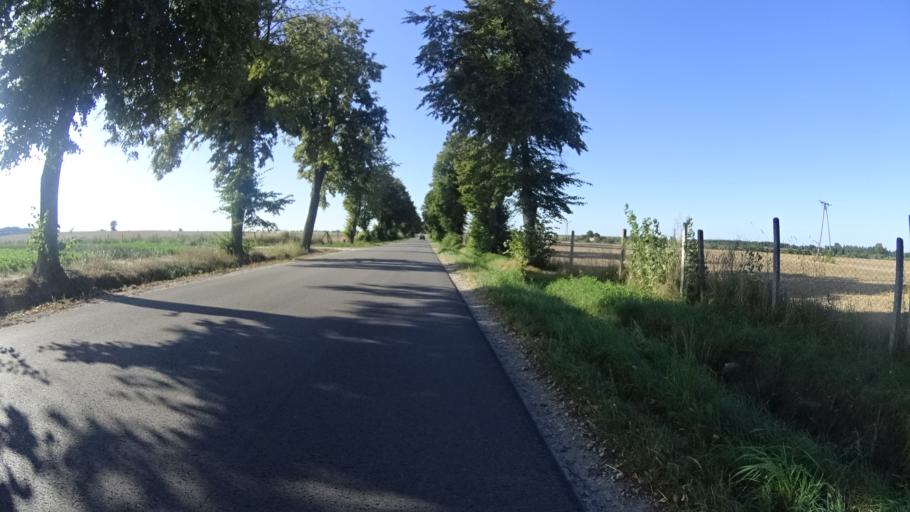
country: PL
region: Masovian Voivodeship
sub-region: Powiat bialobrzeski
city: Wysmierzyce
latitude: 51.6757
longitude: 20.8302
